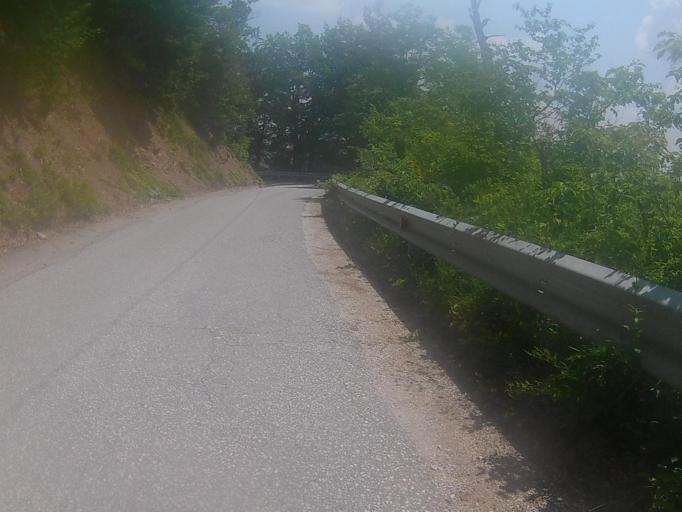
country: SI
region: Maribor
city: Kamnica
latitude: 46.5987
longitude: 15.6025
